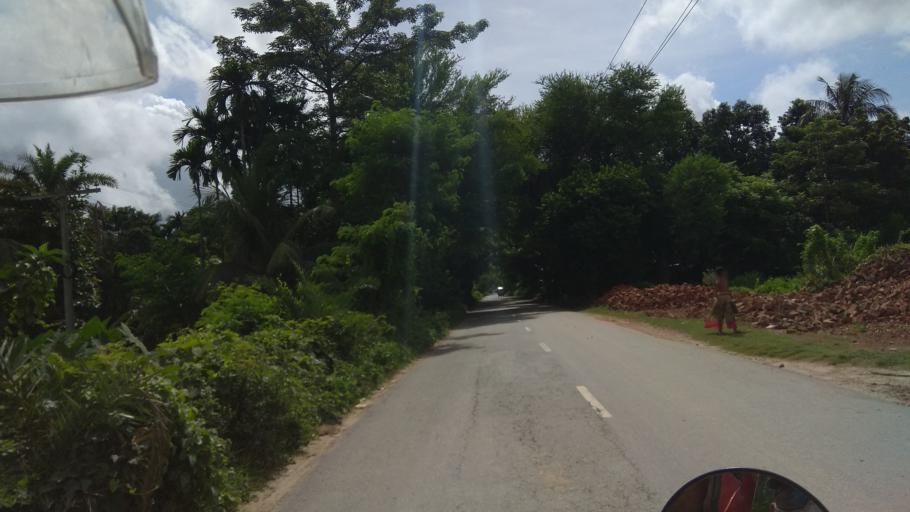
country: BD
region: Khulna
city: Kalia
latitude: 23.1957
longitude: 89.6791
